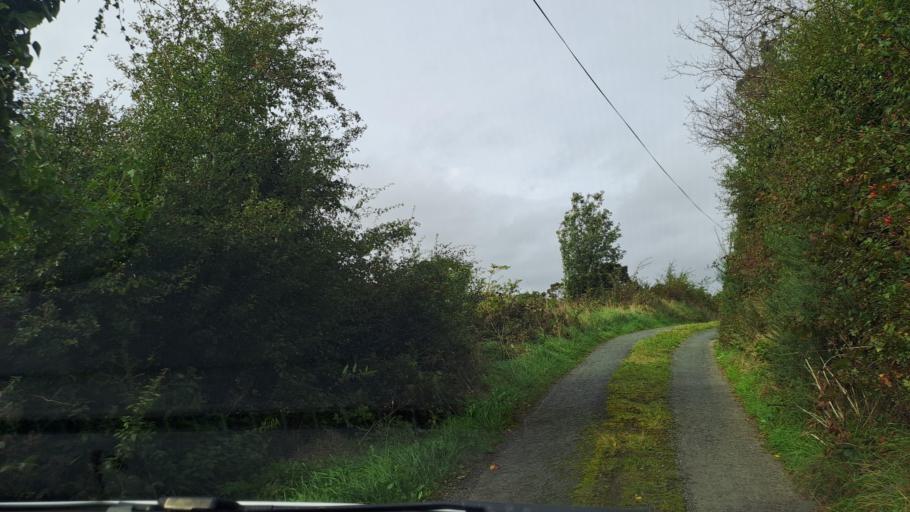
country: IE
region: Ulster
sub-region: An Cabhan
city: Bailieborough
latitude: 54.0016
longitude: -6.9421
